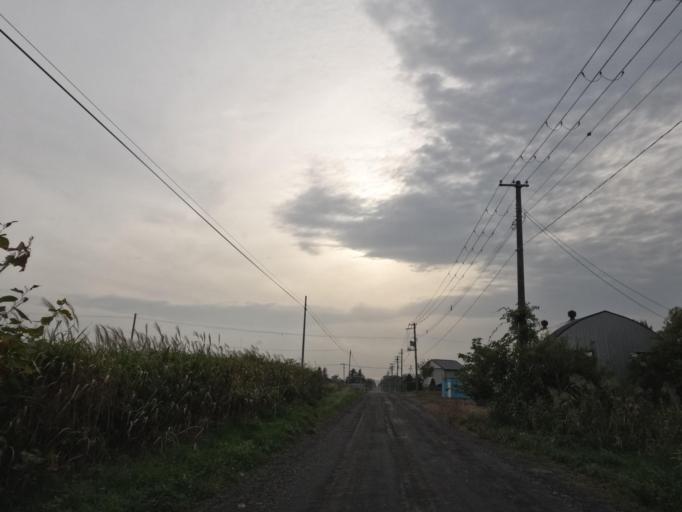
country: JP
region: Hokkaido
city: Date
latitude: 42.4377
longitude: 140.9087
